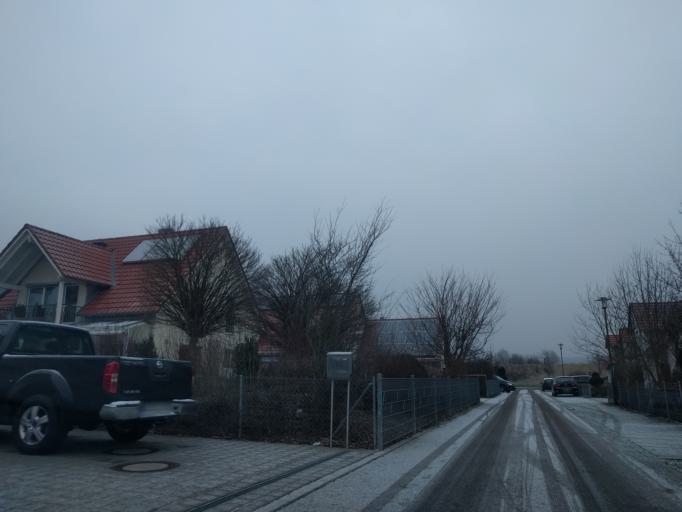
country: DE
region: Bavaria
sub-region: Swabia
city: Donauwoerth
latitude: 48.7188
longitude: 10.7497
